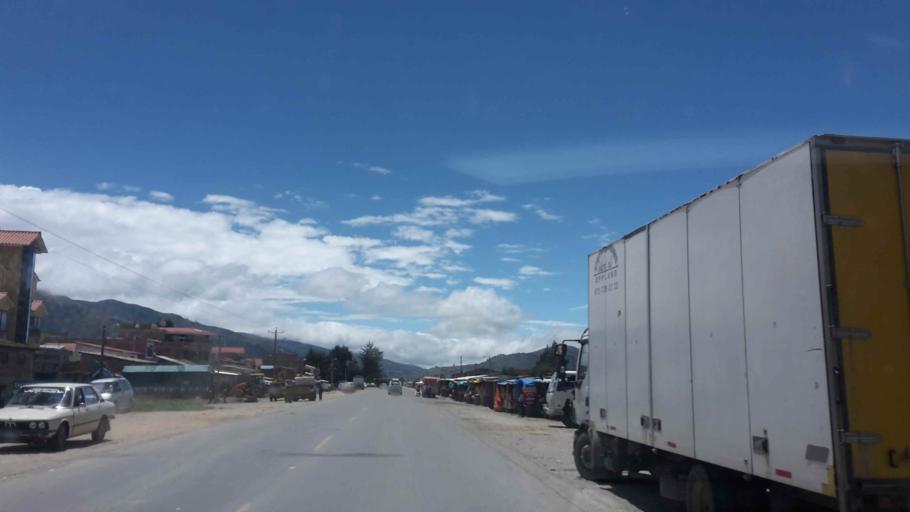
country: BO
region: Cochabamba
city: Colomi
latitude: -17.3331
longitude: -65.8695
